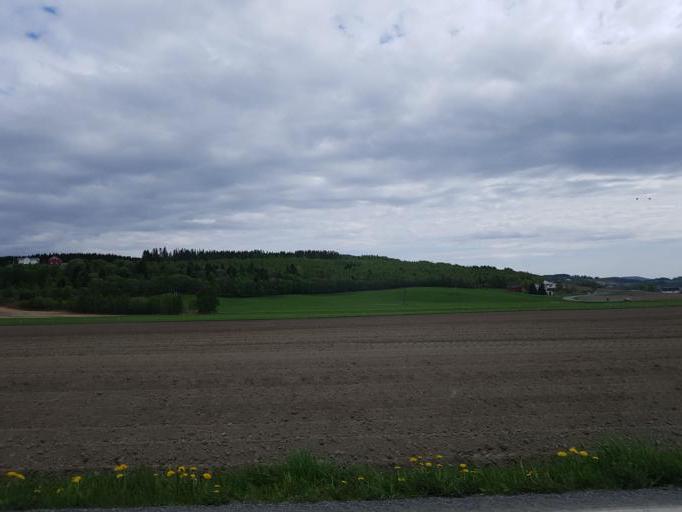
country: NO
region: Nord-Trondelag
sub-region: Levanger
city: Skogn
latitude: 63.6957
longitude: 11.2227
